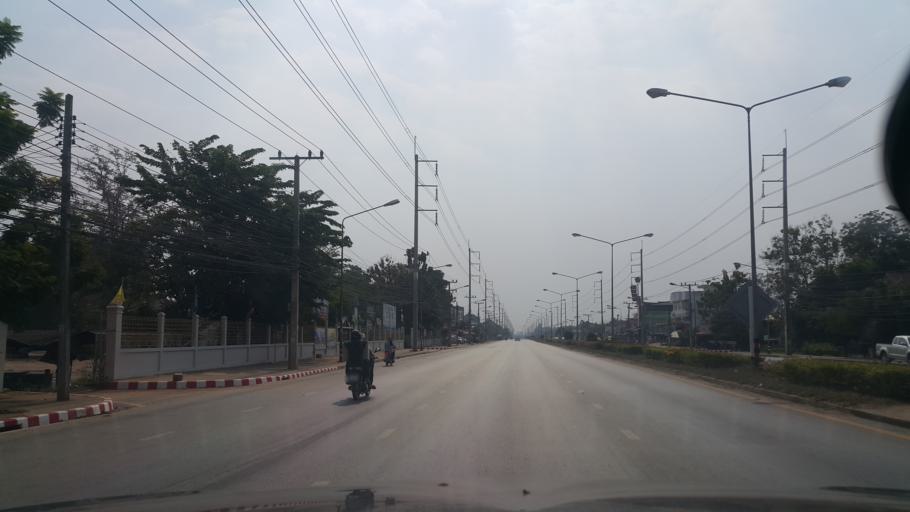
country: TH
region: Phitsanulok
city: Phitsanulok
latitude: 16.8791
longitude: 100.2055
